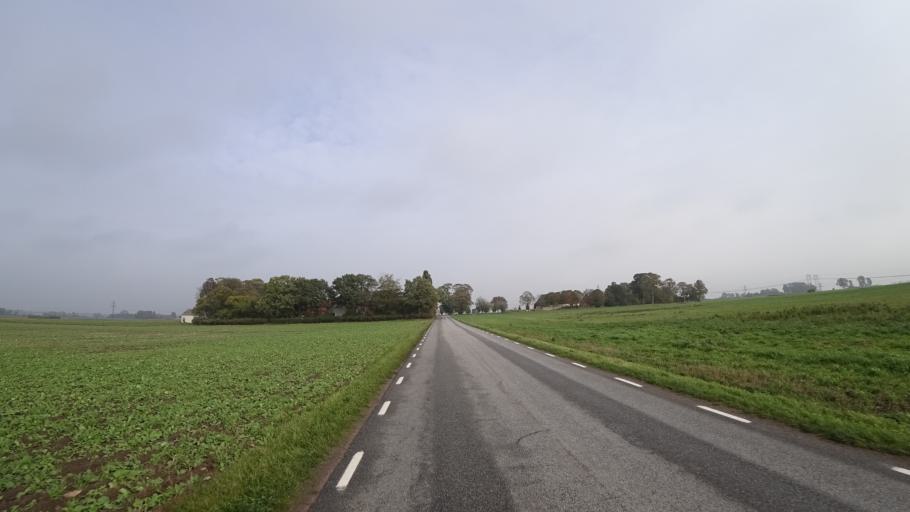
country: SE
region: Skane
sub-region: Kavlinge Kommun
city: Loddekopinge
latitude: 55.7957
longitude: 13.0031
